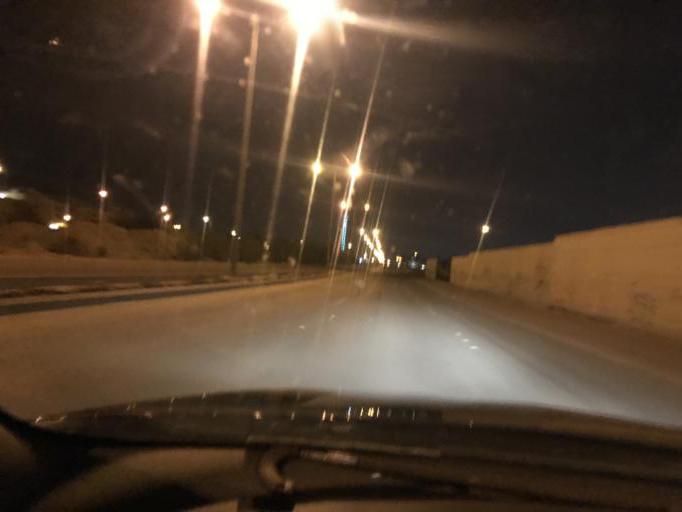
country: SA
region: Ar Riyad
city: Riyadh
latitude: 24.8161
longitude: 46.7185
